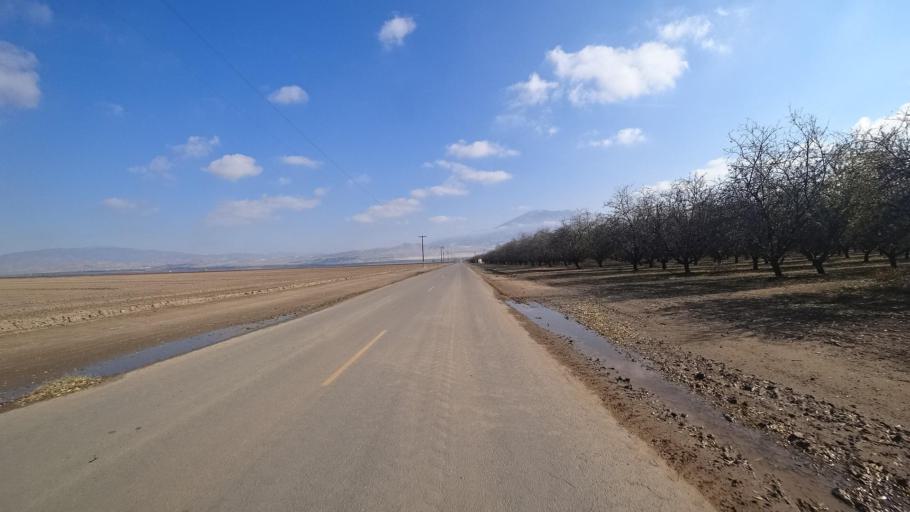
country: US
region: California
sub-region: Kern County
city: Arvin
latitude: 35.2384
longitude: -118.8048
